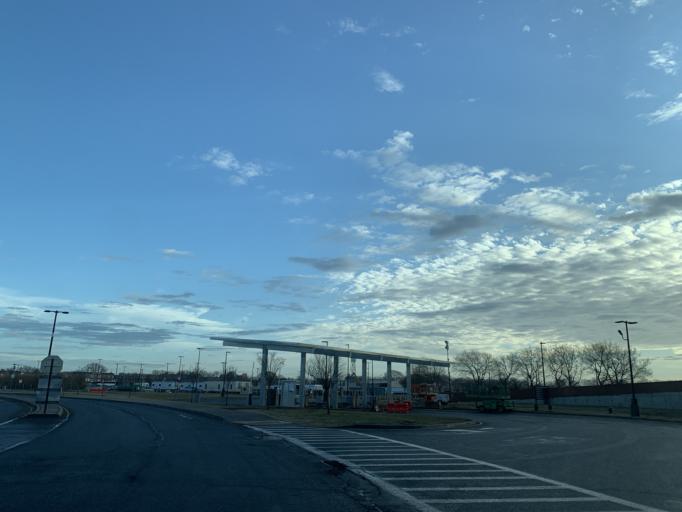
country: US
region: New York
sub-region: Queens County
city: Borough of Queens
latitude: 40.6754
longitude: -73.8320
